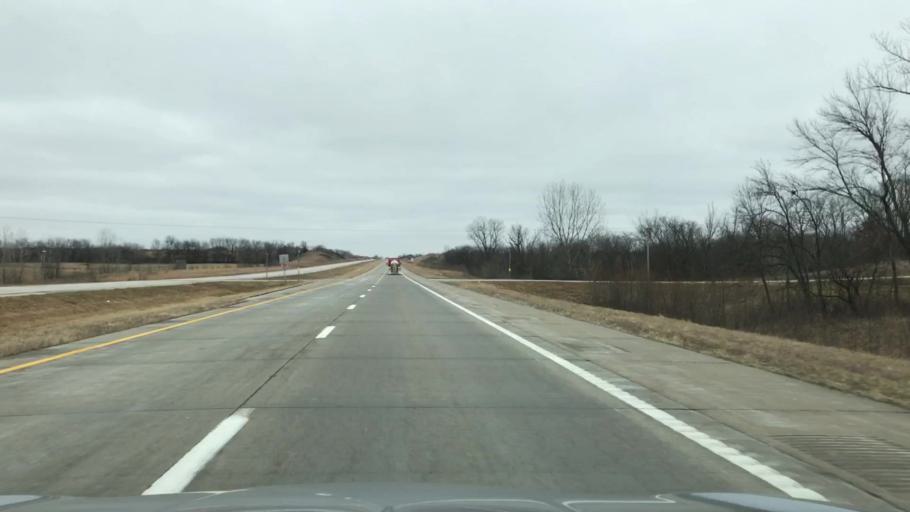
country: US
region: Missouri
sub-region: Caldwell County
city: Hamilton
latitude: 39.7343
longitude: -93.9653
